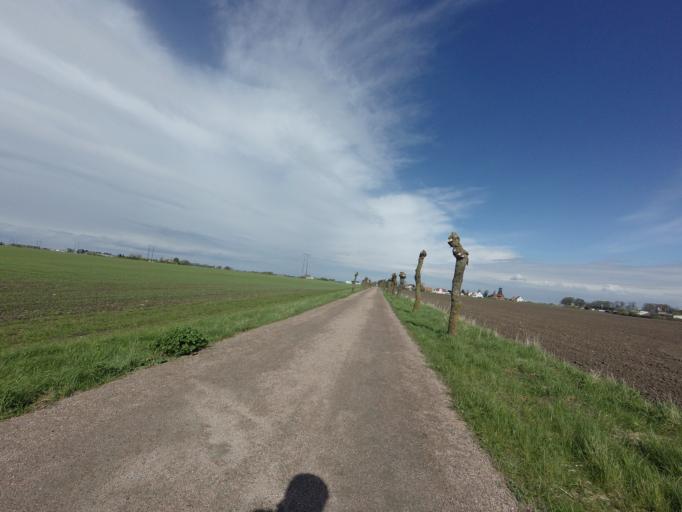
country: SE
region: Skane
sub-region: Malmo
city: Tygelsjo
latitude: 55.5221
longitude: 12.9898
